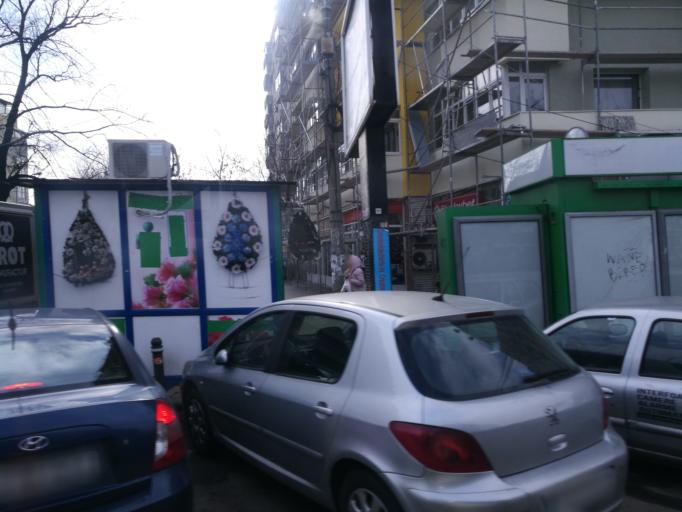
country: RO
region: Bucuresti
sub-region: Municipiul Bucuresti
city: Bucharest
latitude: 44.4527
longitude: 26.1033
